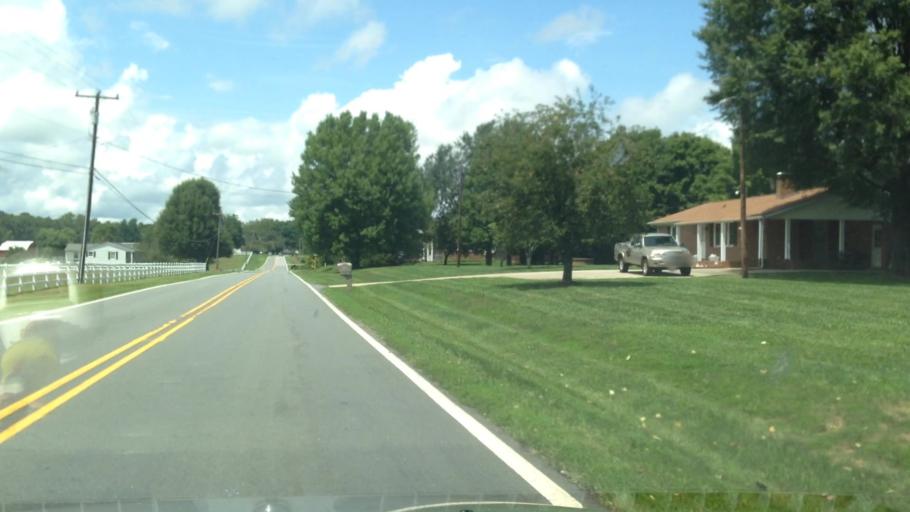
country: US
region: North Carolina
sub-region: Forsyth County
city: Kernersville
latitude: 36.1440
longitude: -80.0834
